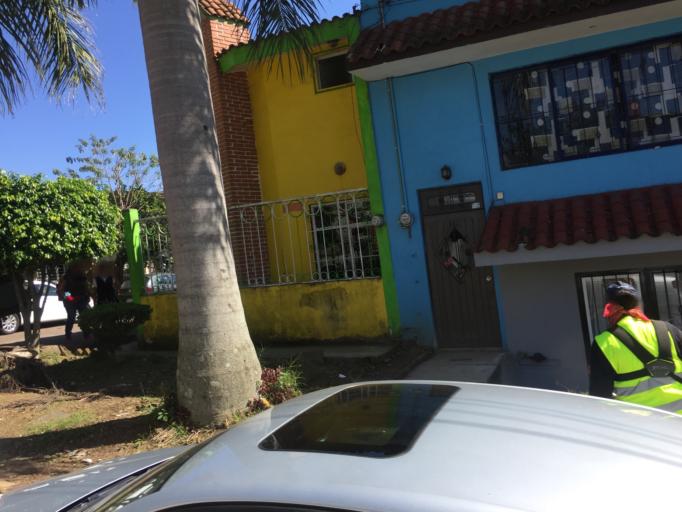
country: MX
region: Veracruz
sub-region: Xalapa
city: Xalapa de Enriquez
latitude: 19.5365
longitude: -96.9106
